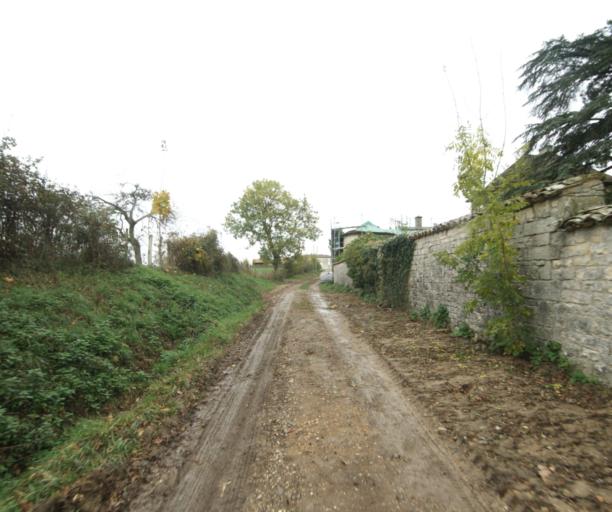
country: FR
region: Rhone-Alpes
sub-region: Departement de l'Ain
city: Pont-de-Vaux
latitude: 46.4634
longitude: 4.8711
